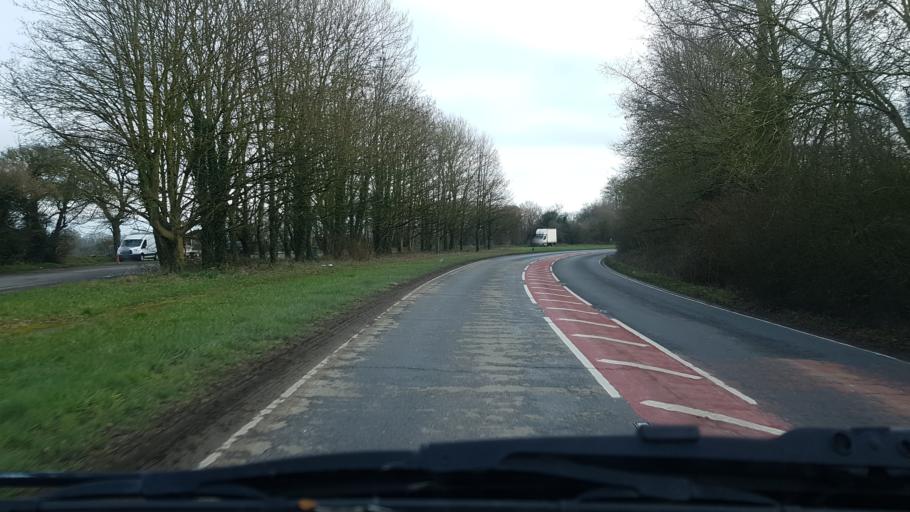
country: GB
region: England
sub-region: Wiltshire
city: Tidworth
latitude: 51.2514
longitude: -1.6001
